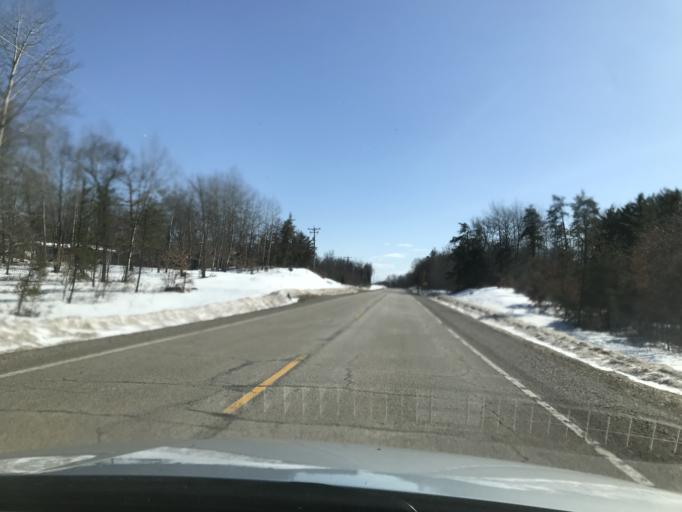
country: US
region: Wisconsin
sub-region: Marinette County
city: Niagara
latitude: 45.3453
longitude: -88.1015
